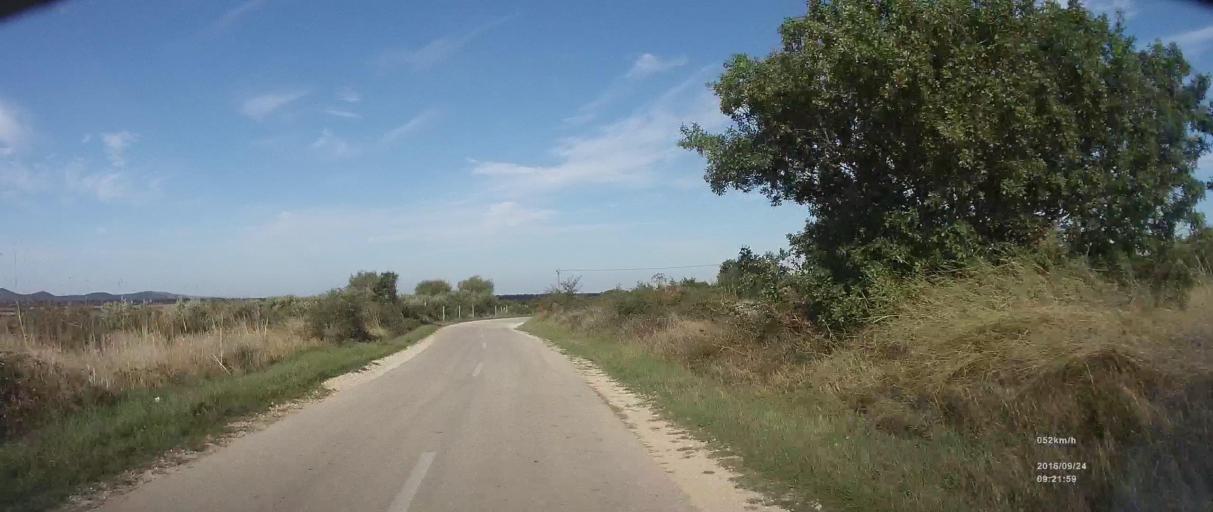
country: HR
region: Zadarska
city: Polaca
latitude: 44.0697
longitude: 15.4833
